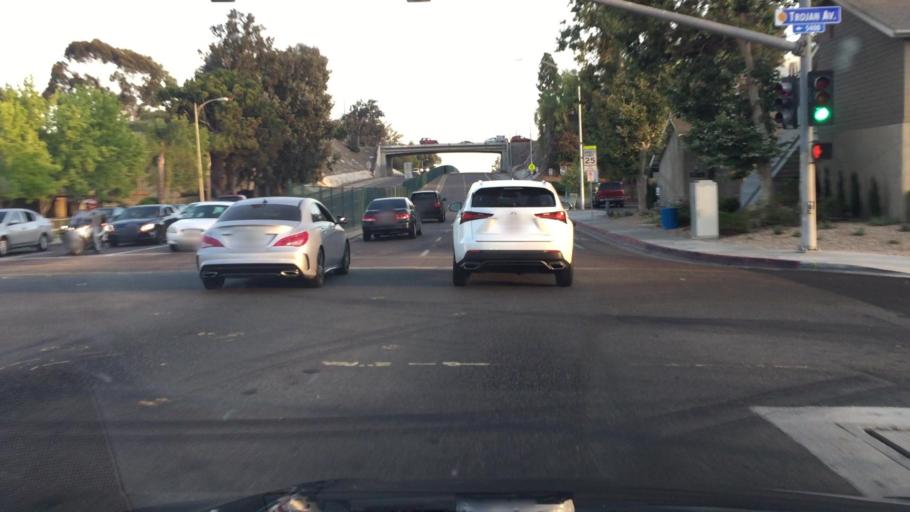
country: US
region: California
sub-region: San Diego County
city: Lemon Grove
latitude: 32.7549
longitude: -117.0795
